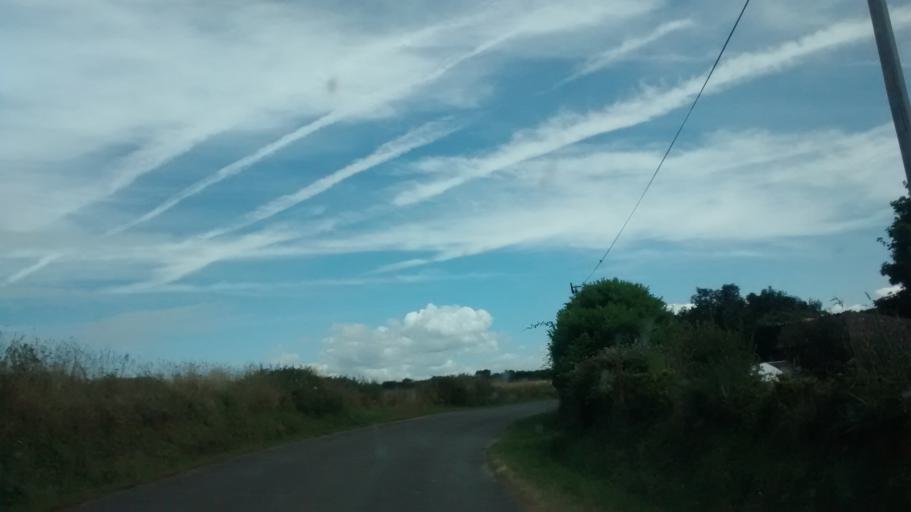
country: FR
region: Brittany
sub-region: Departement du Finistere
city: Plouguerneau
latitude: 48.6227
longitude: -4.4716
